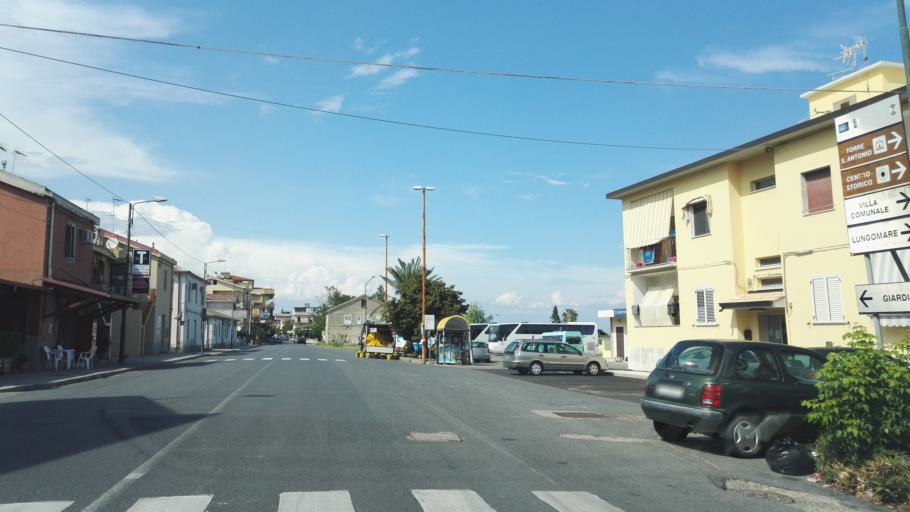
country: IT
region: Calabria
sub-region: Provincia di Catanzaro
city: Santa Caterina dello Ionio Marina
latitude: 38.5299
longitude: 16.5707
